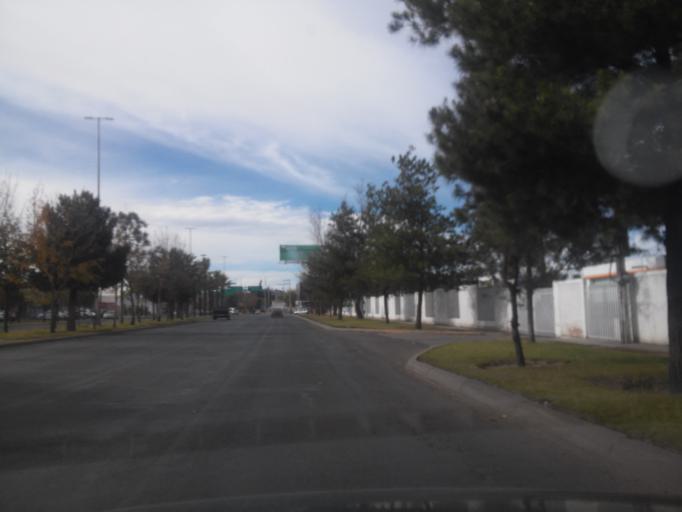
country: MX
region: Durango
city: Victoria de Durango
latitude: 24.0079
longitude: -104.6594
